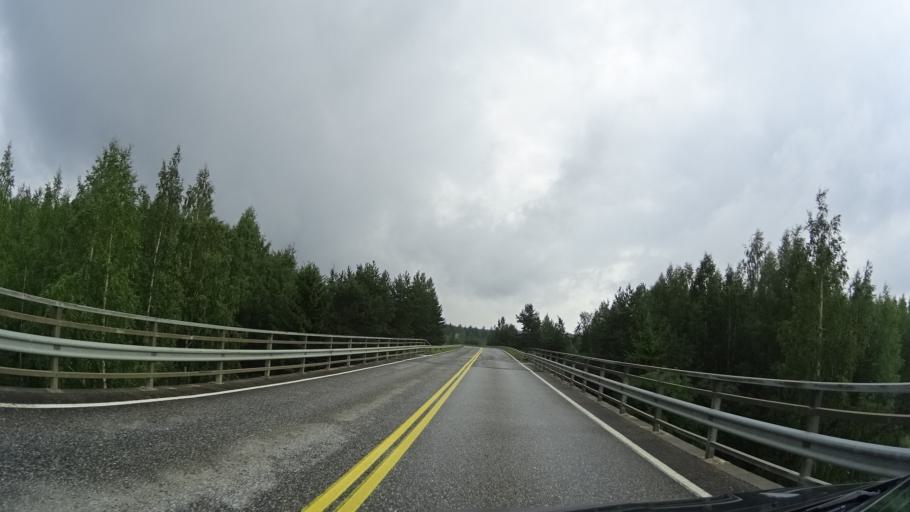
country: FI
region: North Karelia
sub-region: Keski-Karjala
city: Raeaekkylae
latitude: 62.3144
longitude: 29.5144
